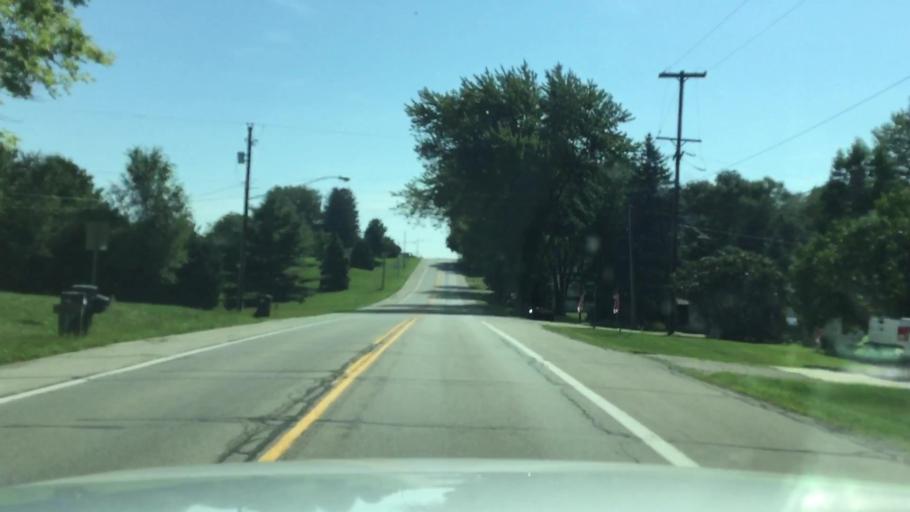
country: US
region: Michigan
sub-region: Lenawee County
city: Manitou Beach-Devils Lake
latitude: 42.0055
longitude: -84.2851
